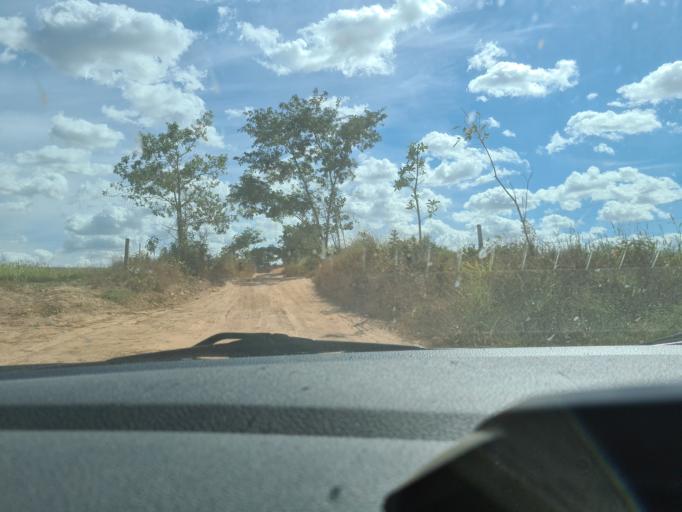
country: BR
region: Goias
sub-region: Silvania
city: Silvania
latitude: -16.5351
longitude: -48.5854
